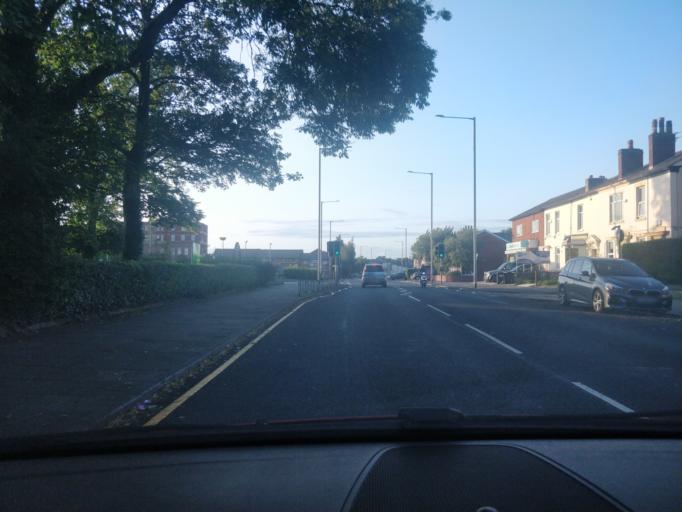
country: GB
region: England
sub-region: Lancashire
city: Preston
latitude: 53.7646
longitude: -2.6912
